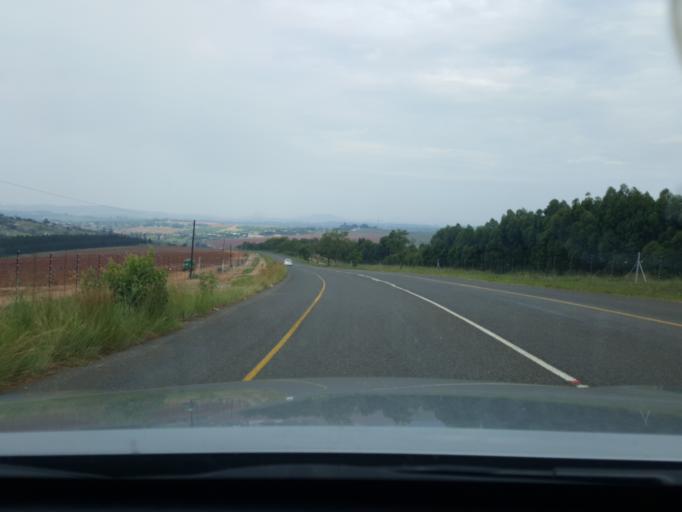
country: ZA
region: Mpumalanga
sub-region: Ehlanzeni District
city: White River
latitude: -25.2851
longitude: 30.9669
